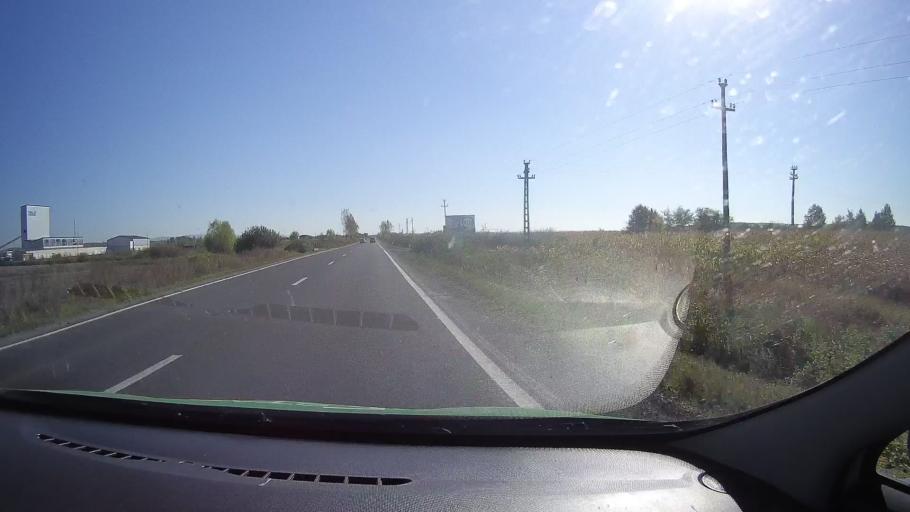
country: RO
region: Satu Mare
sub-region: Oras Ardud
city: Ardud
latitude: 47.6562
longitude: 22.8768
